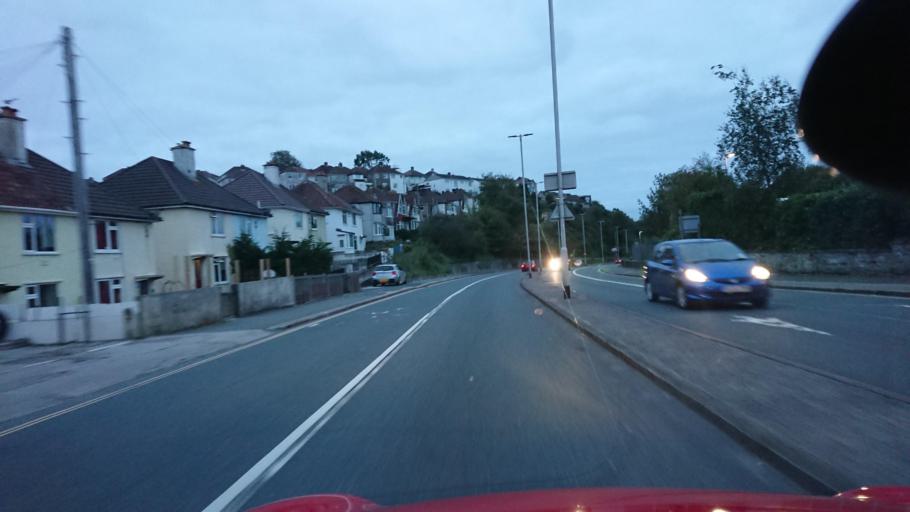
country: GB
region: England
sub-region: Cornwall
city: Torpoint
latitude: 50.4010
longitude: -4.1846
